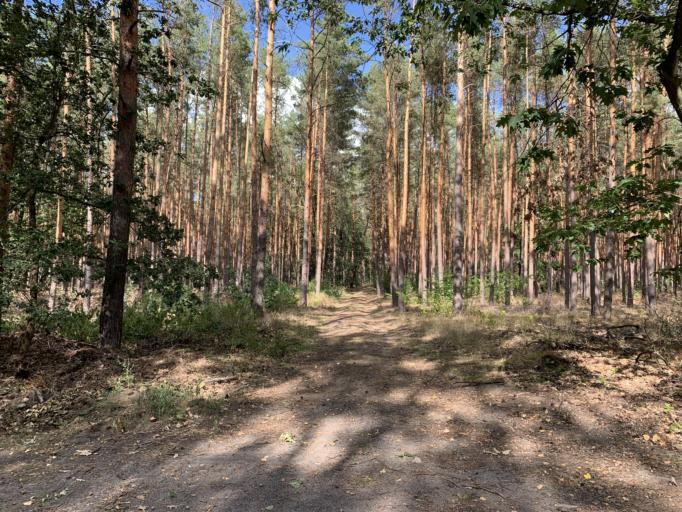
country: DE
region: Brandenburg
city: Michendorf
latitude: 52.3099
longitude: 12.9997
